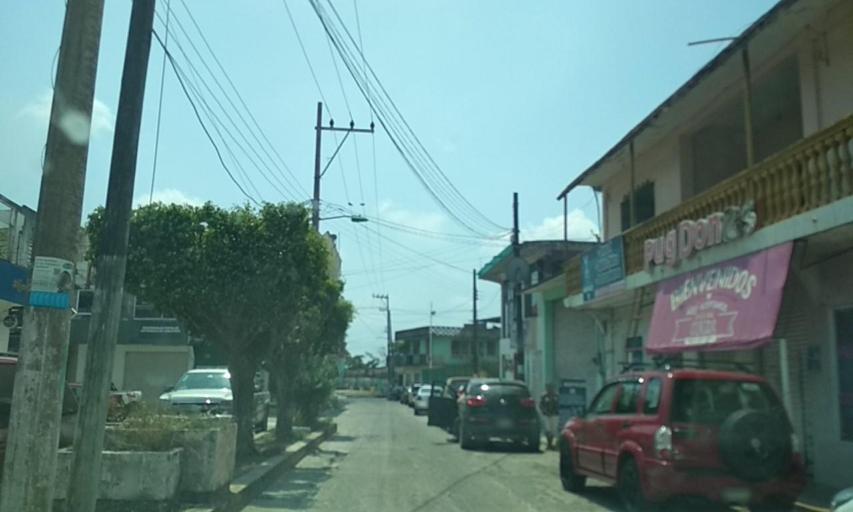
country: MX
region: Veracruz
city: Las Choapas
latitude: 17.9075
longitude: -94.0896
